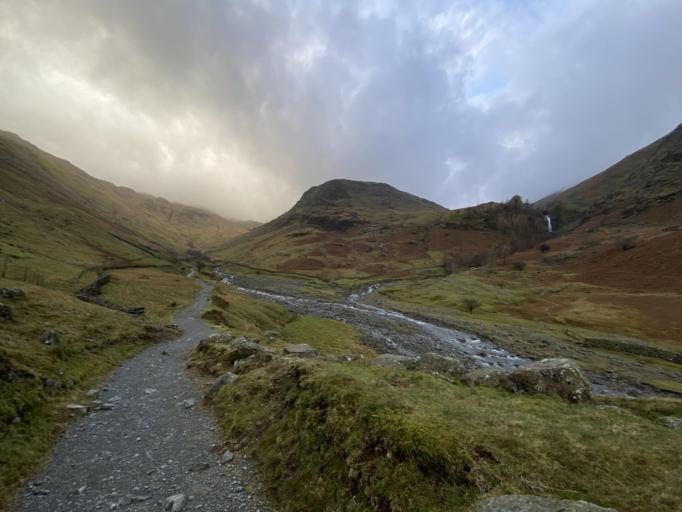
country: GB
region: England
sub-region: Cumbria
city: Keswick
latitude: 54.4906
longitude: -3.1830
